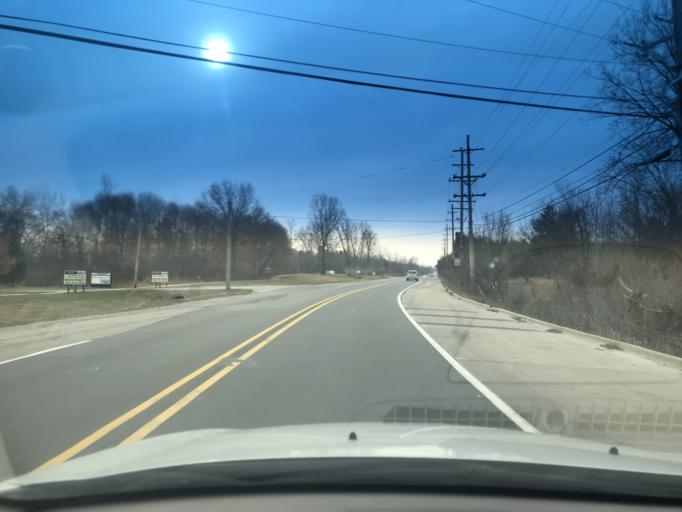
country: US
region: Michigan
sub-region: Macomb County
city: Shelby
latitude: 42.7110
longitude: -83.0551
